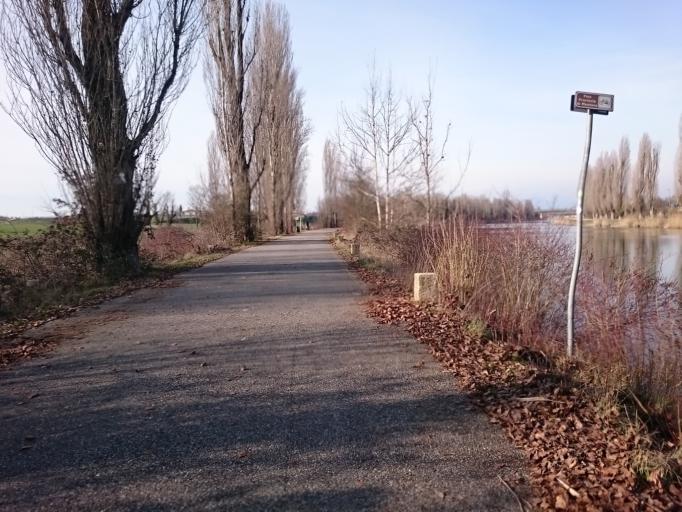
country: IT
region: Lombardy
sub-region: Provincia di Mantova
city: Ponti sul Mincio
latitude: 45.4220
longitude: 10.7011
